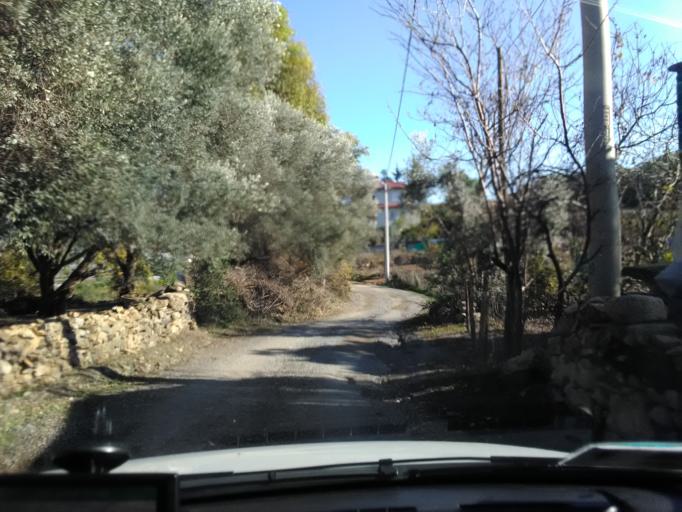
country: TR
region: Antalya
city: Gazipasa
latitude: 36.2469
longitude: 32.3402
